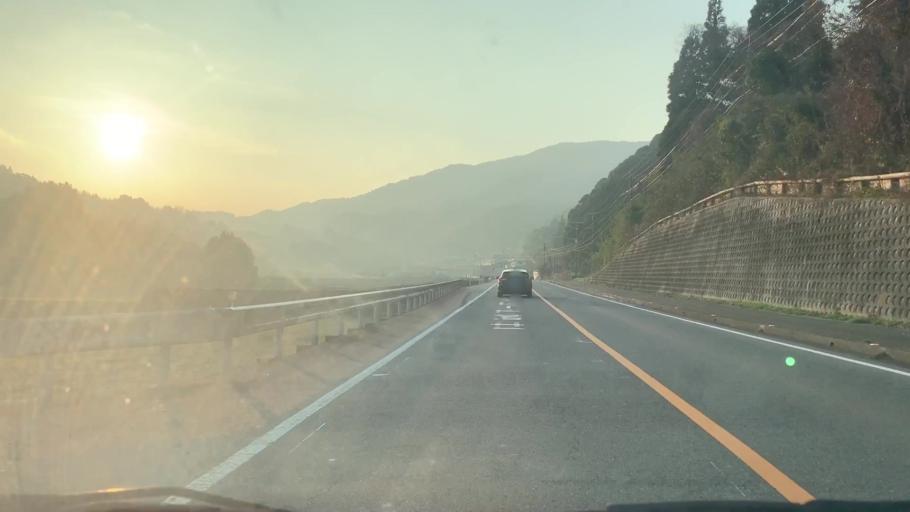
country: JP
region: Saga Prefecture
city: Takeocho-takeo
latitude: 33.2638
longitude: 130.0401
